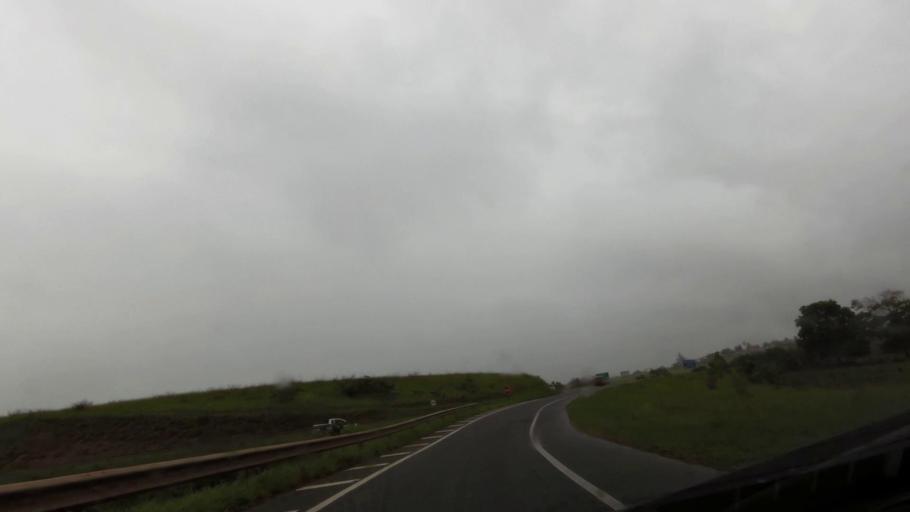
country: BR
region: Espirito Santo
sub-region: Guarapari
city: Guarapari
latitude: -20.7402
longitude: -40.5493
